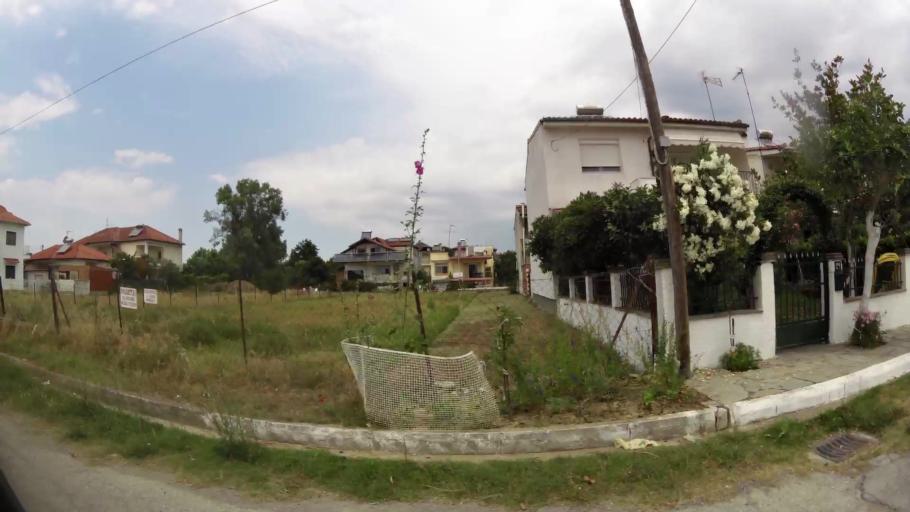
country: GR
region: Central Macedonia
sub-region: Nomos Pierias
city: Kallithea
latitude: 40.2733
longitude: 22.5715
